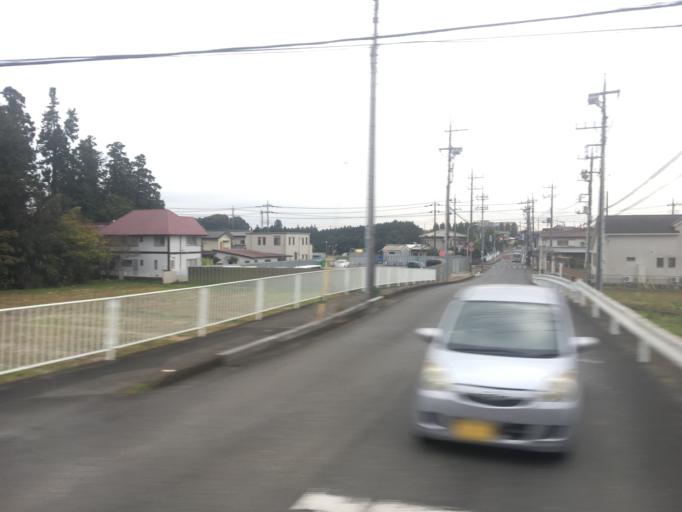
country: JP
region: Saitama
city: Hanno
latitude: 35.8646
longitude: 139.3324
